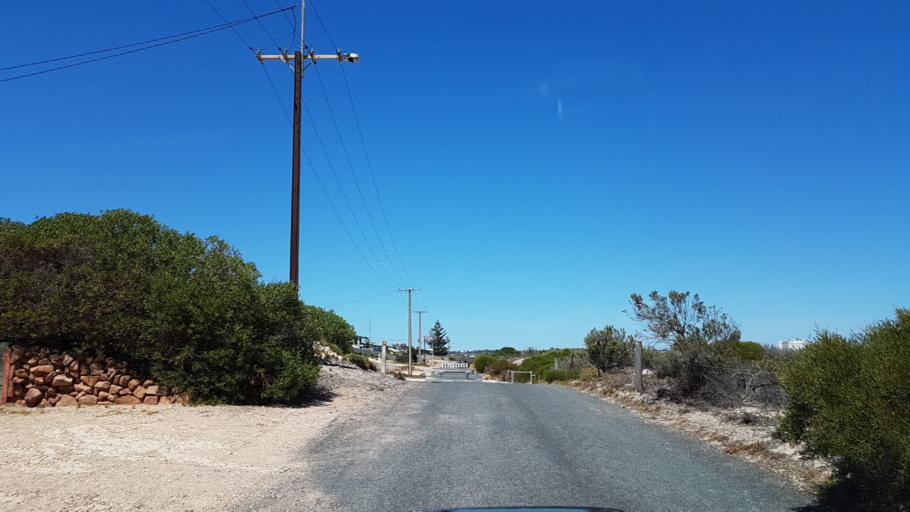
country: AU
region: South Australia
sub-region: Copper Coast
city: Wallaroo
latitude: -33.8983
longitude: 137.6282
